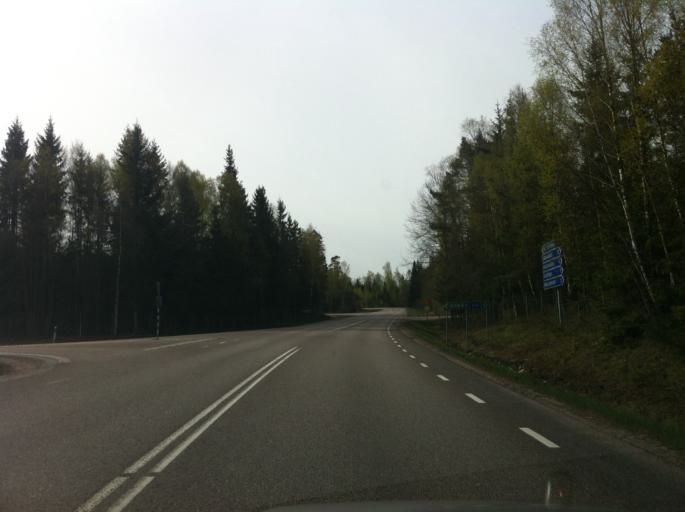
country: SE
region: Vaestra Goetaland
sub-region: Bollebygds Kommun
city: Bollebygd
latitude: 57.6671
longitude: 12.6049
